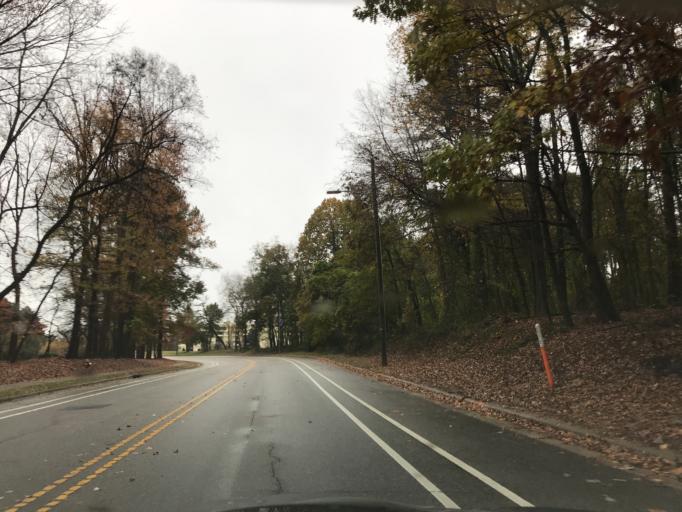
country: US
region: North Carolina
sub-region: Wake County
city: West Raleigh
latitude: 35.8325
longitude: -78.6229
